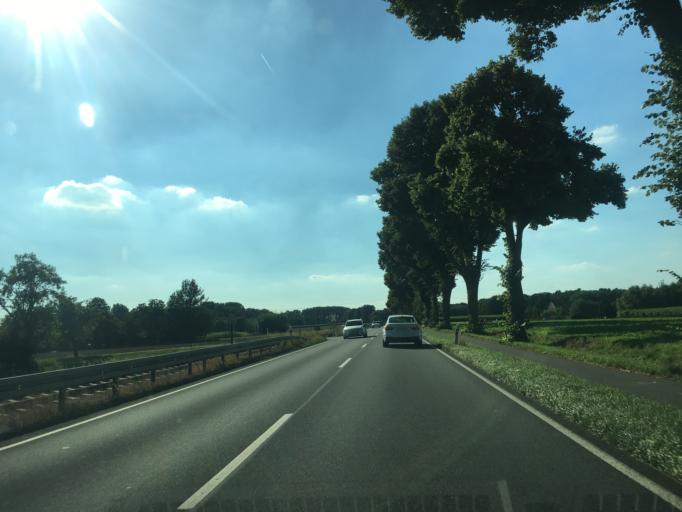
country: DE
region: North Rhine-Westphalia
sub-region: Regierungsbezirk Munster
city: Everswinkel
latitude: 51.9595
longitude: 7.9120
